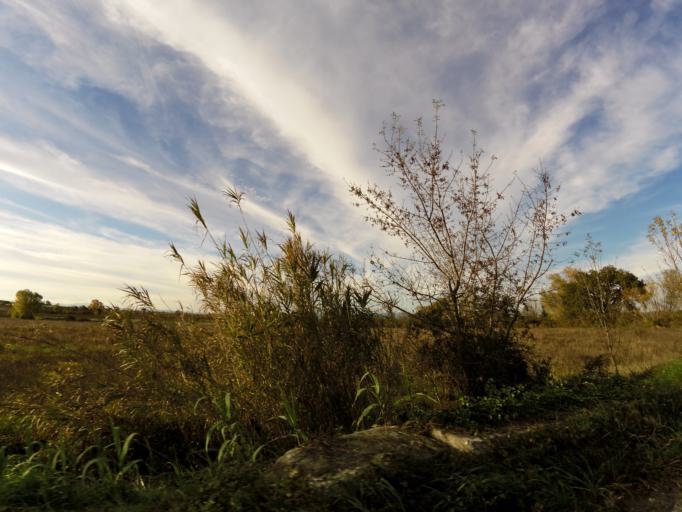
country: FR
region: Languedoc-Roussillon
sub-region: Departement du Gard
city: Ledignan
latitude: 43.9931
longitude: 4.1141
